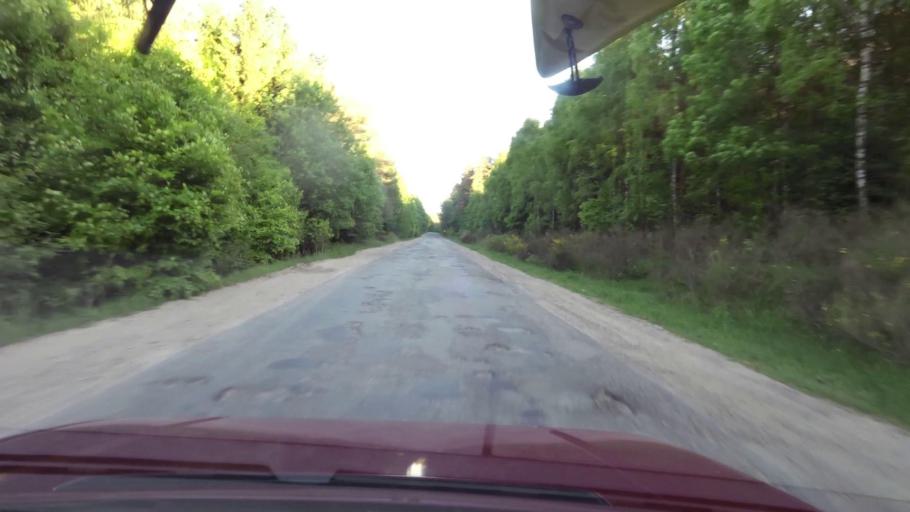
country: PL
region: West Pomeranian Voivodeship
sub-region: Powiat szczecinecki
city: Bialy Bor
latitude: 53.9287
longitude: 16.8013
